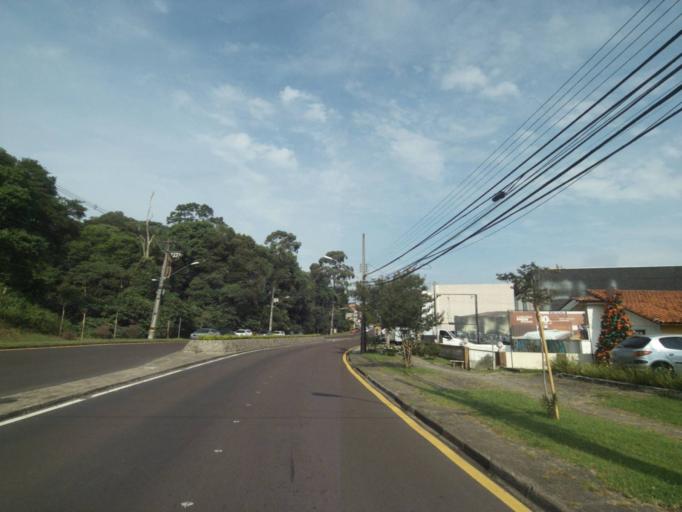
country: BR
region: Parana
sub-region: Curitiba
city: Curitiba
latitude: -25.4132
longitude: -49.3156
